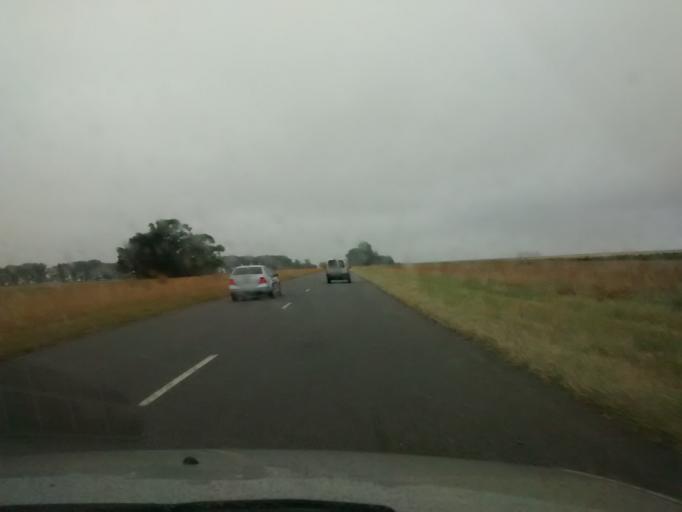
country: AR
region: Buenos Aires
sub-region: Partido de Ayacucho
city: Ayacucho
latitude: -37.4717
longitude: -58.4784
